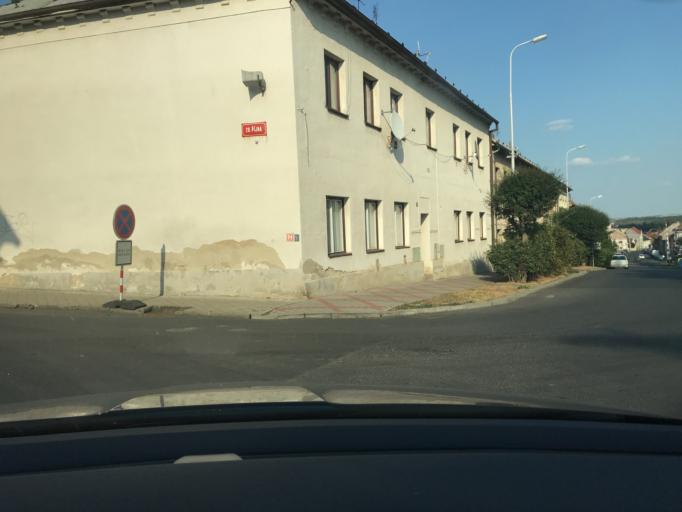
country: CZ
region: Ustecky
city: Postoloprty
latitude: 50.3615
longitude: 13.6914
